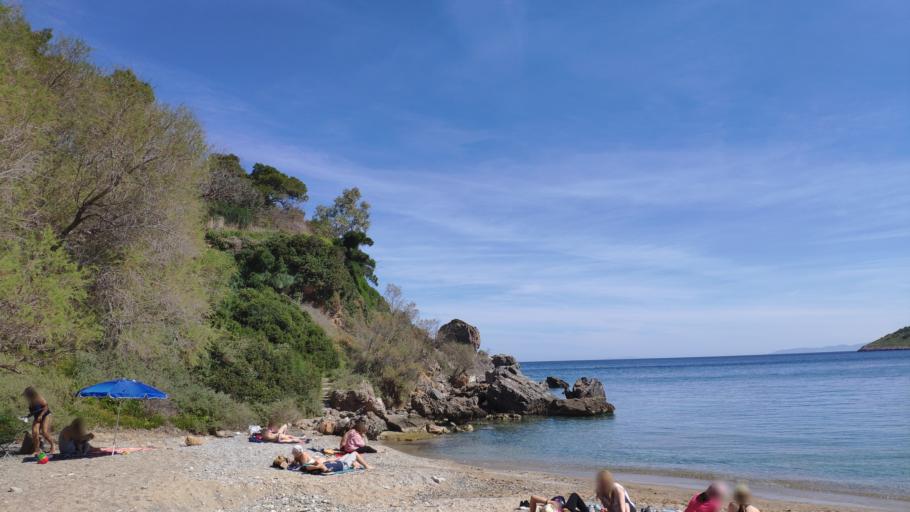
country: GR
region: Attica
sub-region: Nomarchia Anatolikis Attikis
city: Limin Mesoyaias
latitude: 37.8936
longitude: 24.0332
